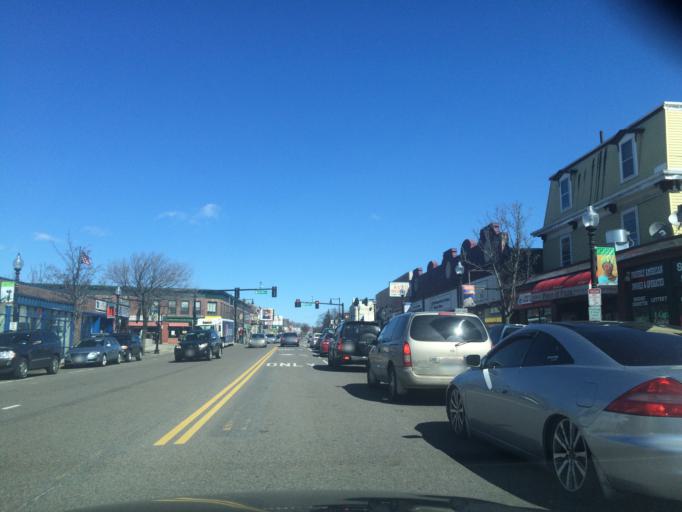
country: US
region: Massachusetts
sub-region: Norfolk County
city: Dedham
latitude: 42.2551
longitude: -71.1243
